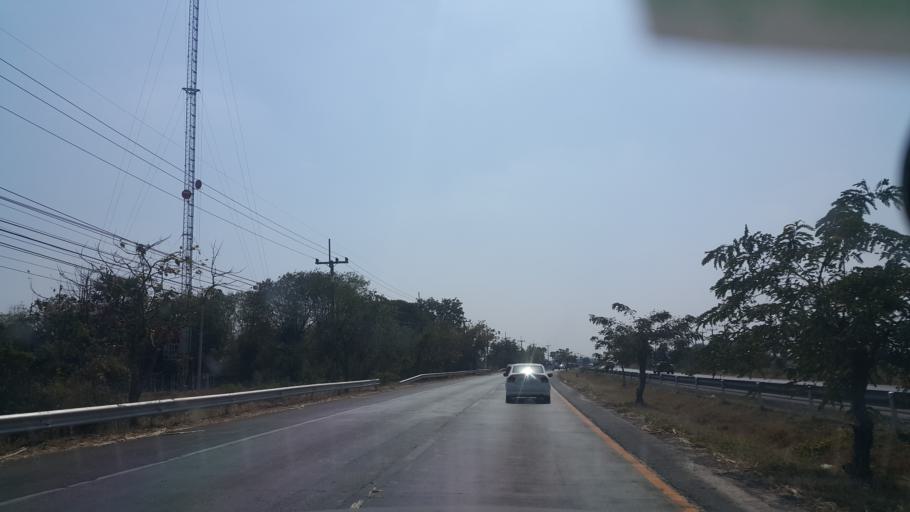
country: TH
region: Nakhon Ratchasima
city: Sida
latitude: 15.5213
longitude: 102.5414
